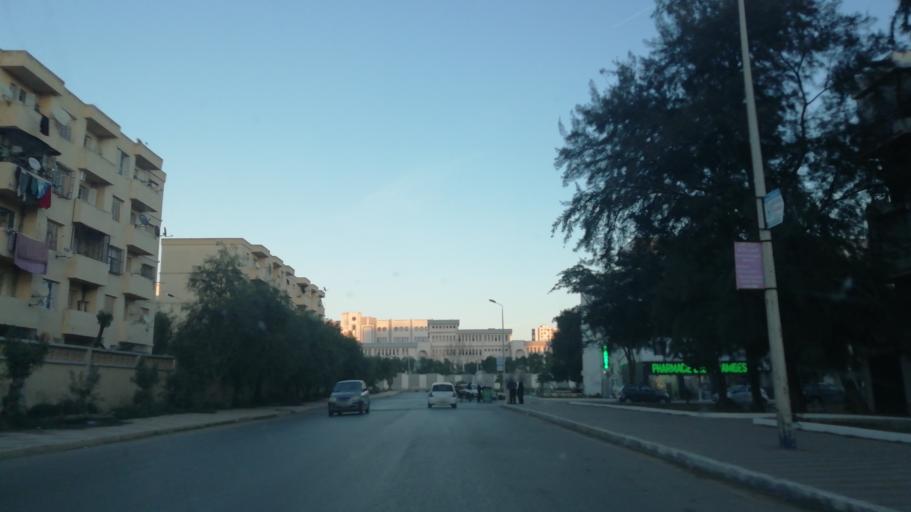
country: DZ
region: Oran
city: Bir el Djir
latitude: 35.6984
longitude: -0.5869
